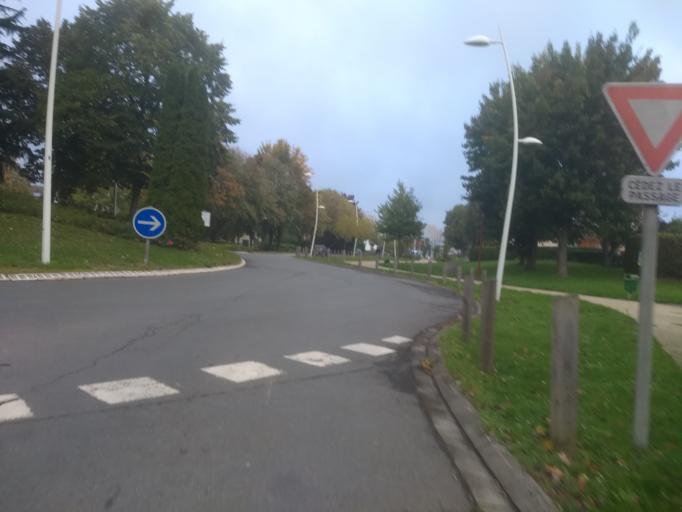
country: FR
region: Nord-Pas-de-Calais
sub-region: Departement du Pas-de-Calais
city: Saint-Nicolas
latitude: 50.3021
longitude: 2.7864
